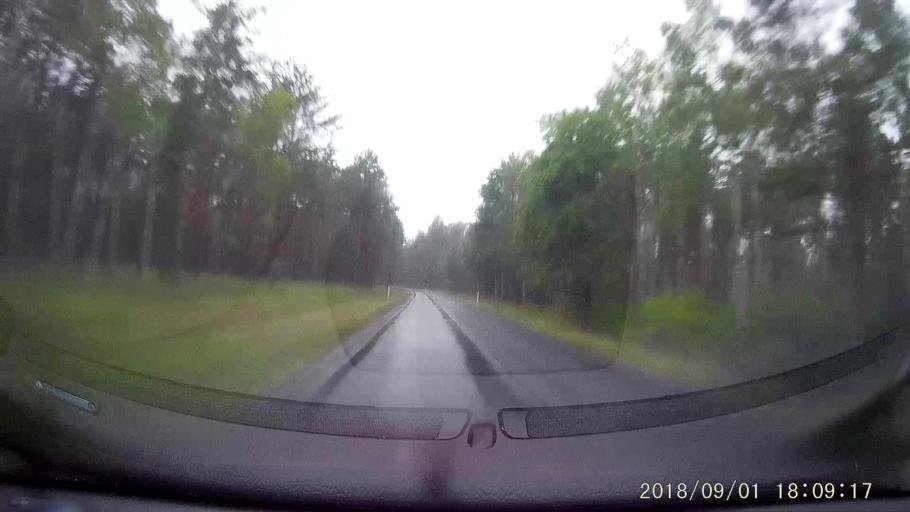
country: PL
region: Lubusz
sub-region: Powiat zaganski
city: Gozdnica
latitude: 51.3420
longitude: 15.1096
